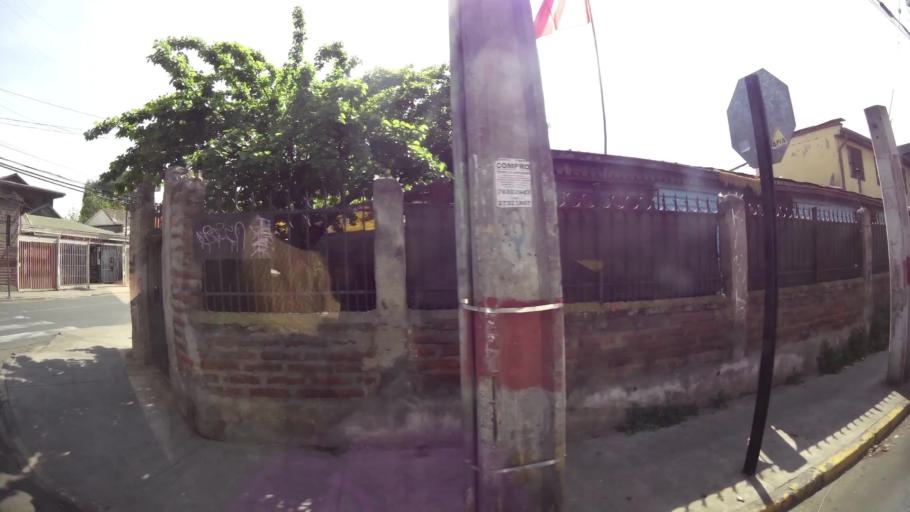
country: CL
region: Santiago Metropolitan
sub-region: Provincia de Santiago
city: Lo Prado
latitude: -33.4341
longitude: -70.7668
